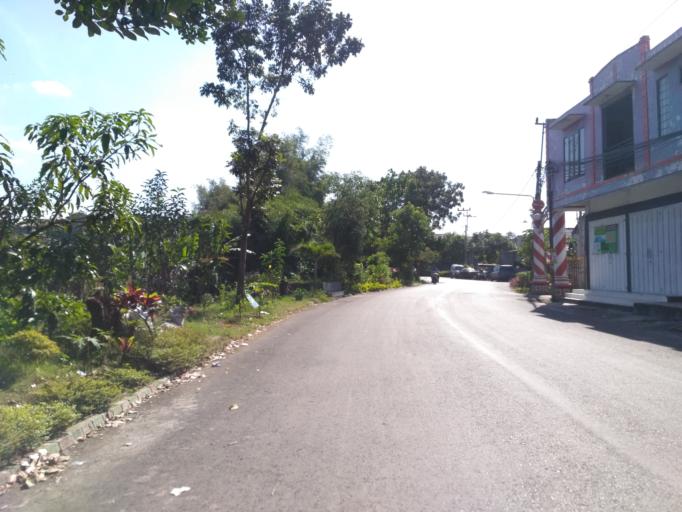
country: ID
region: East Java
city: Singosari
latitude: -7.9100
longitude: 112.6645
